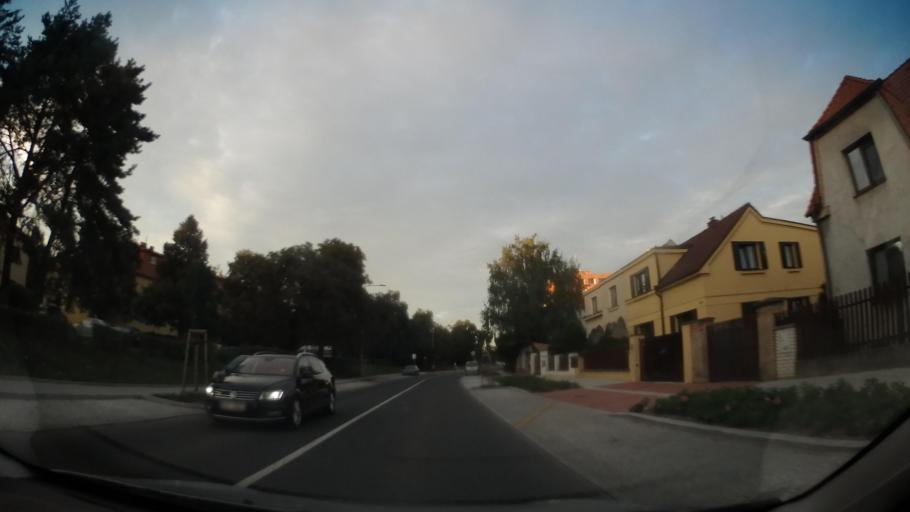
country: CZ
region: Central Bohemia
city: Lysa nad Labem
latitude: 50.2071
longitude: 14.8437
